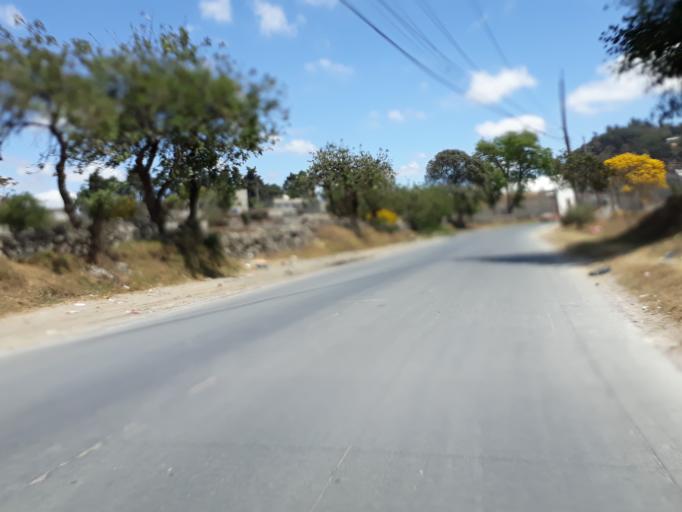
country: GT
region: Quetzaltenango
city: Quetzaltenango
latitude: 14.8193
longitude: -91.5404
